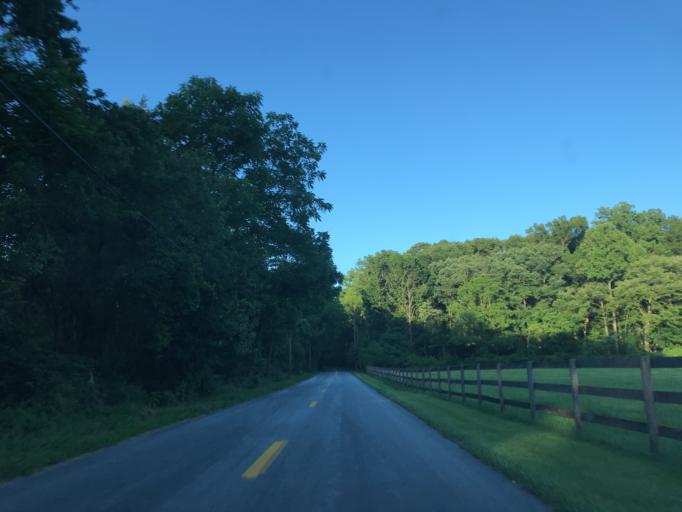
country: US
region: Maryland
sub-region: Baltimore County
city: Hunt Valley
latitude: 39.5633
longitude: -76.6966
